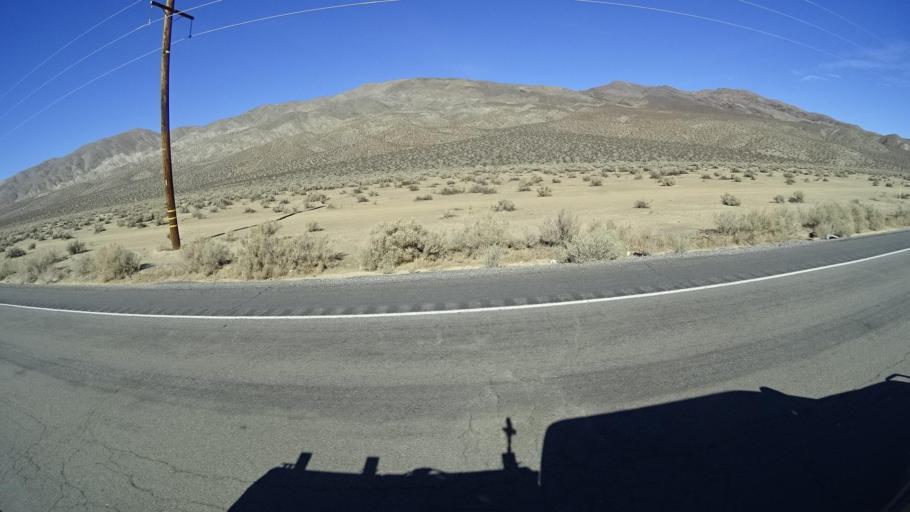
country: US
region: California
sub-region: Kern County
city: Inyokern
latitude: 35.3839
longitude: -117.8256
